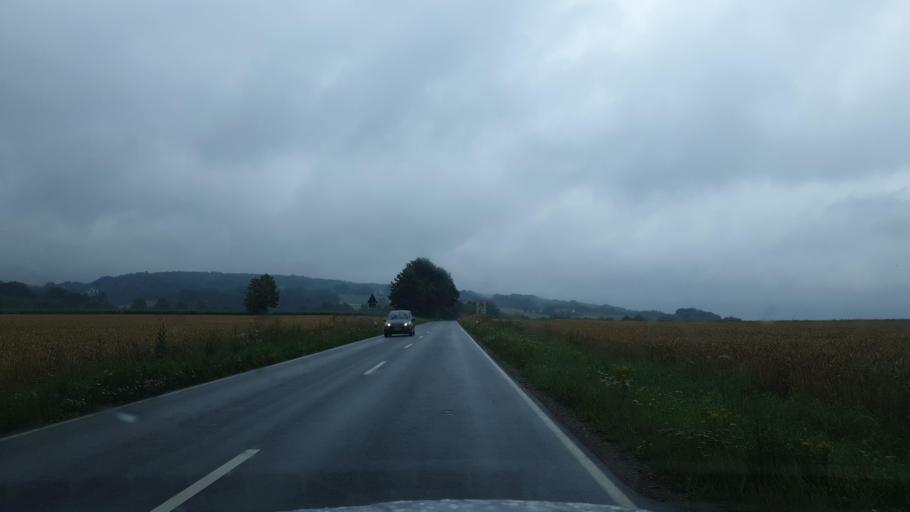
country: DE
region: North Rhine-Westphalia
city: Loehne
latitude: 52.1648
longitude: 8.6836
